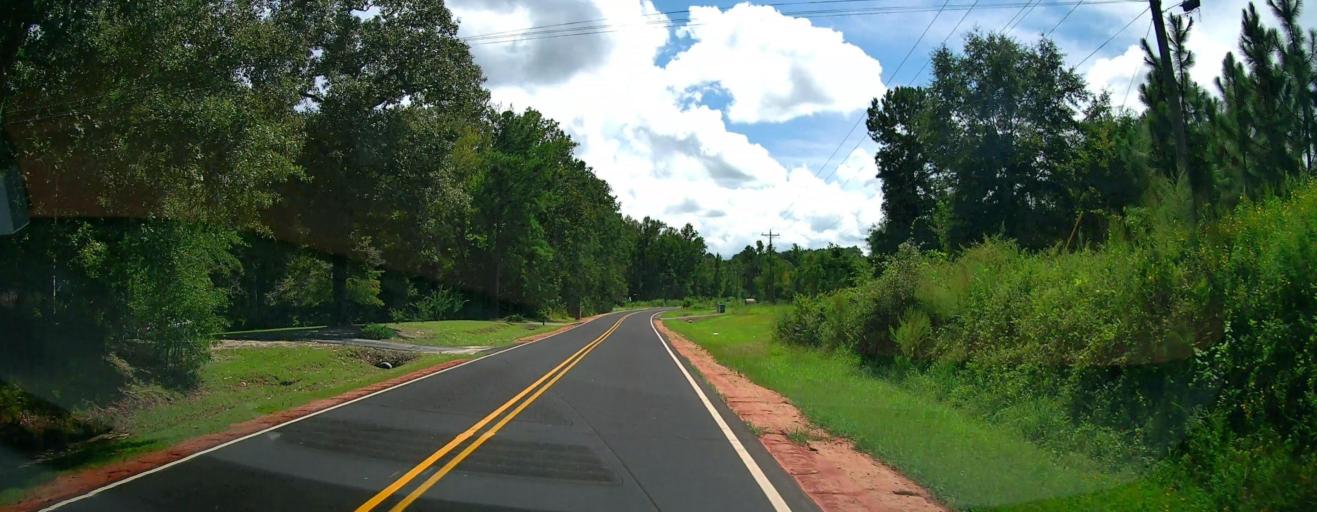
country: US
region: Georgia
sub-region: Peach County
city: Fort Valley
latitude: 32.4806
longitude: -83.8648
